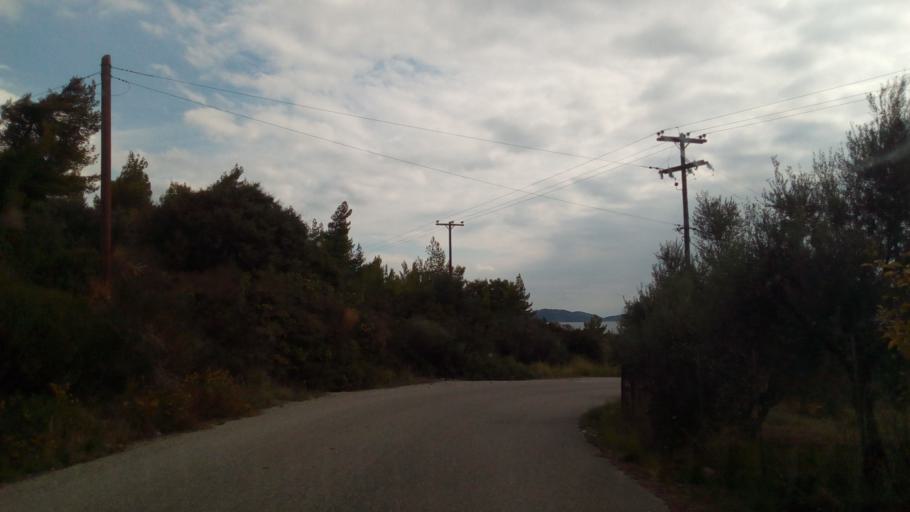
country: GR
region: West Greece
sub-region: Nomos Achaias
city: Kamarai
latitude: 38.3953
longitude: 22.0181
